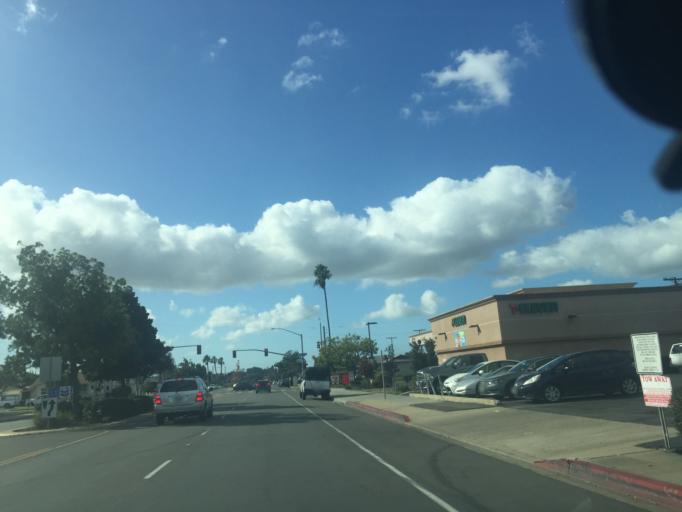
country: US
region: California
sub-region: San Diego County
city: La Mesa
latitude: 32.7915
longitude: -117.0821
